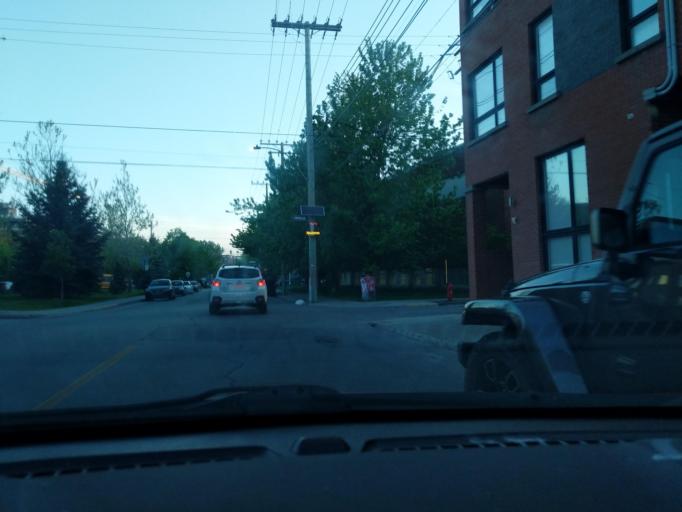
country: CA
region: Quebec
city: Westmount
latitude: 45.4732
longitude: -73.5829
